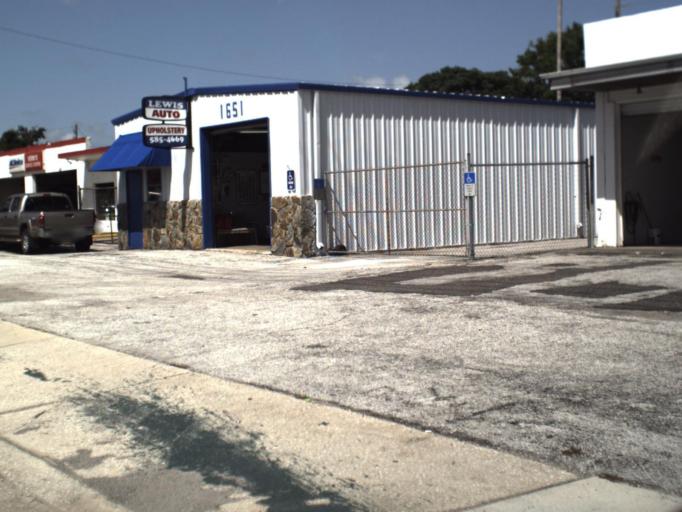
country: US
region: Florida
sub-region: Pinellas County
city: Belleair
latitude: 27.9362
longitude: -82.7873
